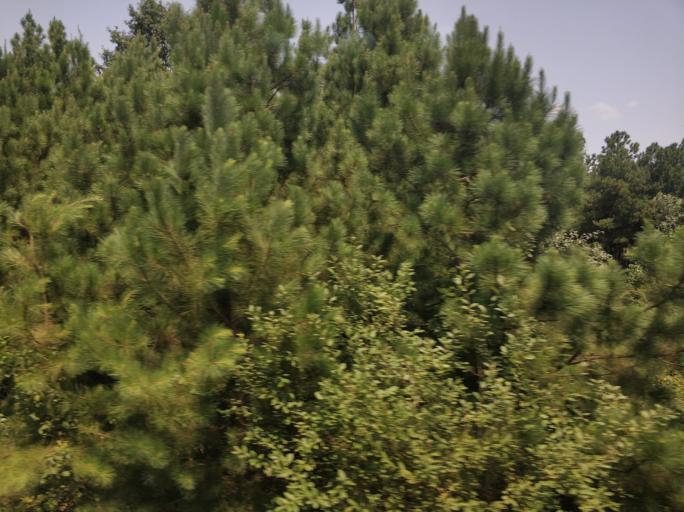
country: IR
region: Gilan
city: Rasht
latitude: 37.1854
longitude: 49.6046
